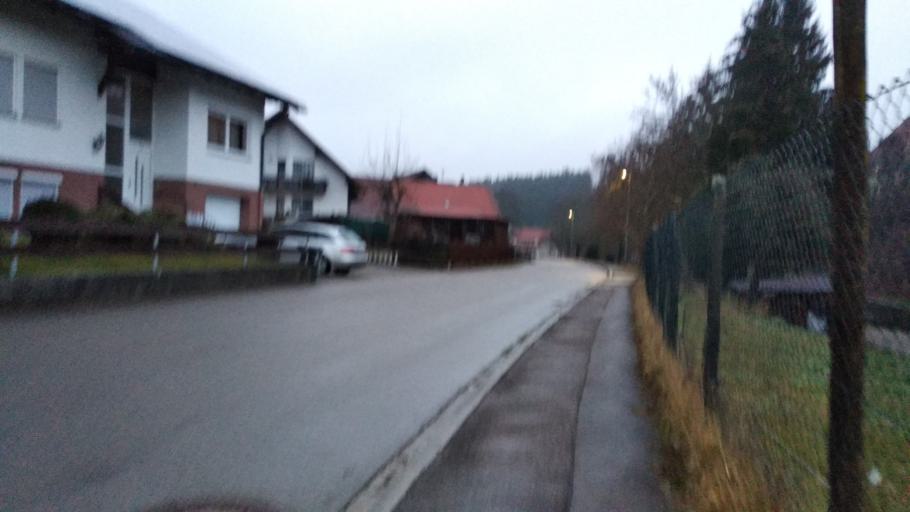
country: DE
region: Bavaria
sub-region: Swabia
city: Lautrach
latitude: 47.8881
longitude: 10.1352
